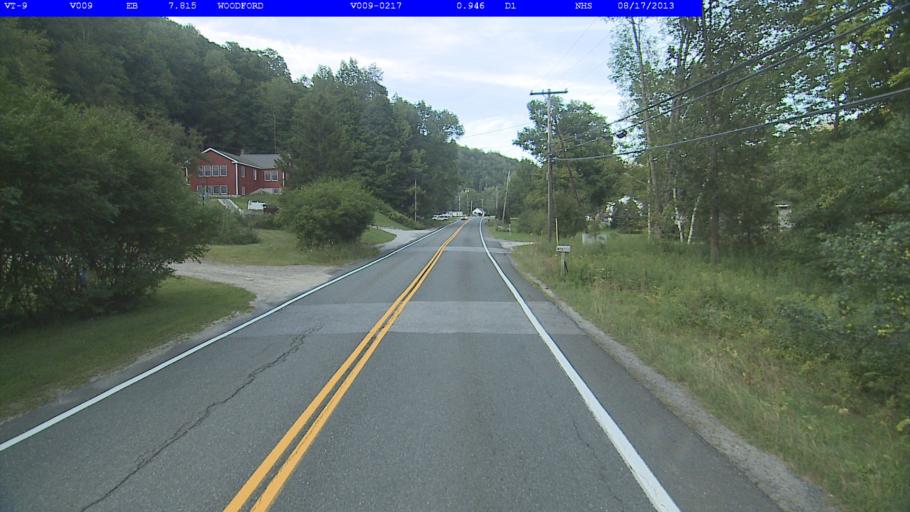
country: US
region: Vermont
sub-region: Bennington County
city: Bennington
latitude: 42.8931
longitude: -73.1373
